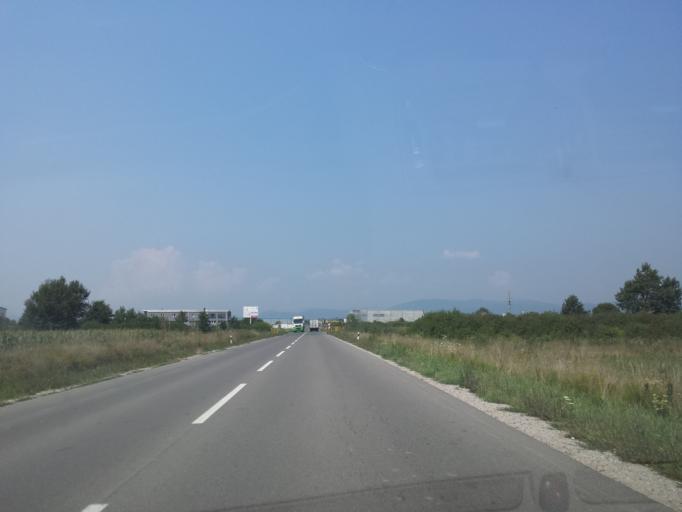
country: HR
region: Zagrebacka
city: Jastrebarsko
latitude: 45.6484
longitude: 15.6680
